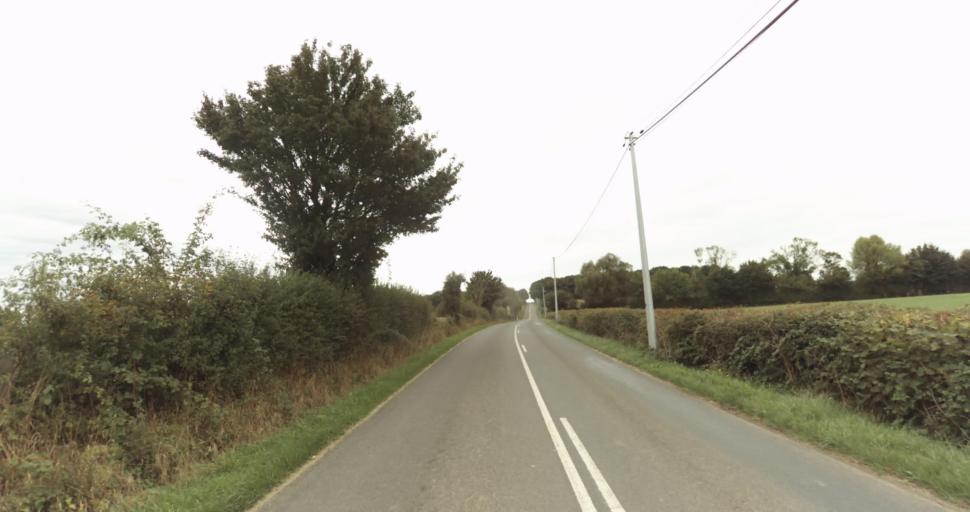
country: FR
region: Lower Normandy
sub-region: Departement de l'Orne
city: Gace
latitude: 48.6910
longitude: 0.2881
